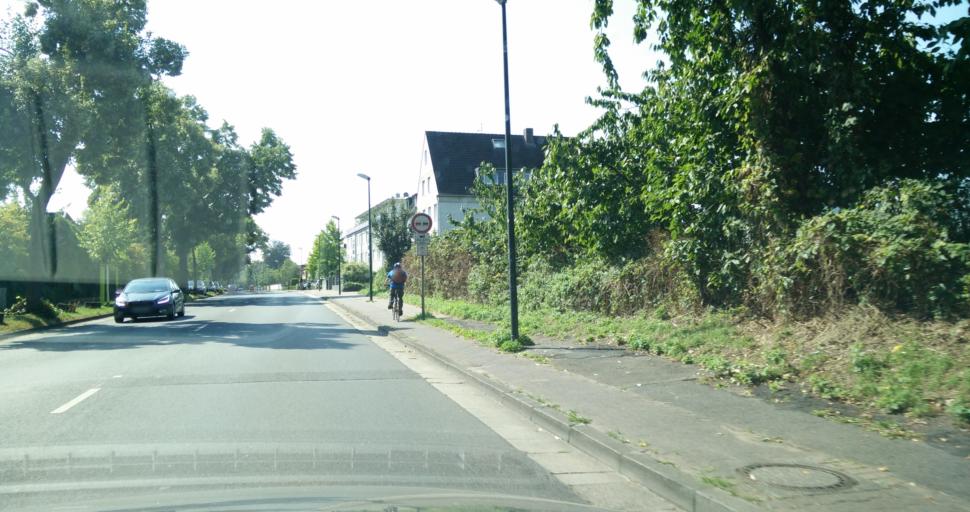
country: DE
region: North Rhine-Westphalia
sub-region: Regierungsbezirk Dusseldorf
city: Meerbusch
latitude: 51.3127
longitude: 6.7436
